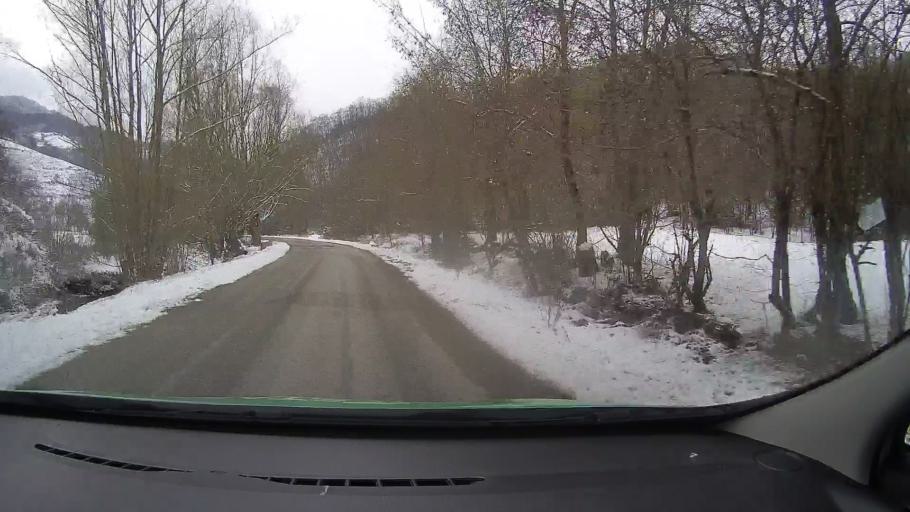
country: RO
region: Hunedoara
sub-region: Comuna Balsa
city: Balsa
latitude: 46.0596
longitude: 23.0935
